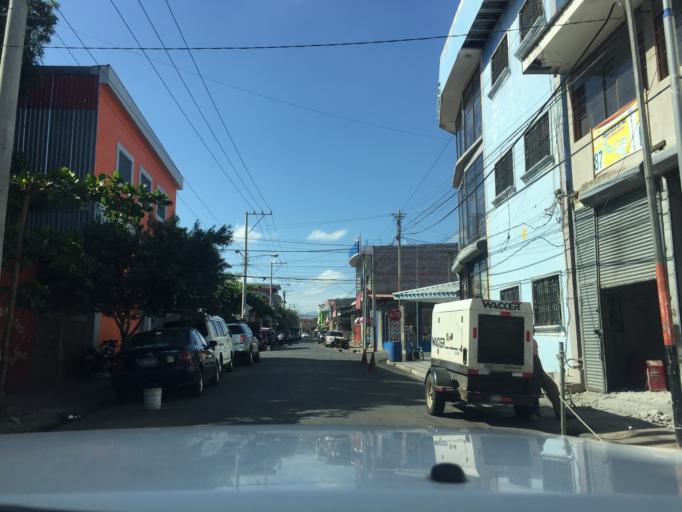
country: NI
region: Managua
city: Managua
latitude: 12.1506
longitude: -86.2560
